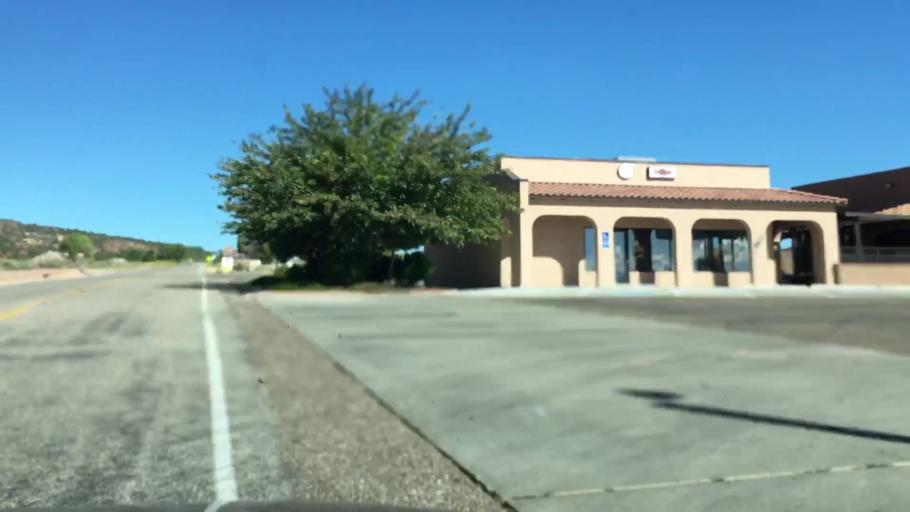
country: US
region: Arizona
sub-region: Coconino County
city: Fredonia
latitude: 36.8581
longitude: -112.7355
